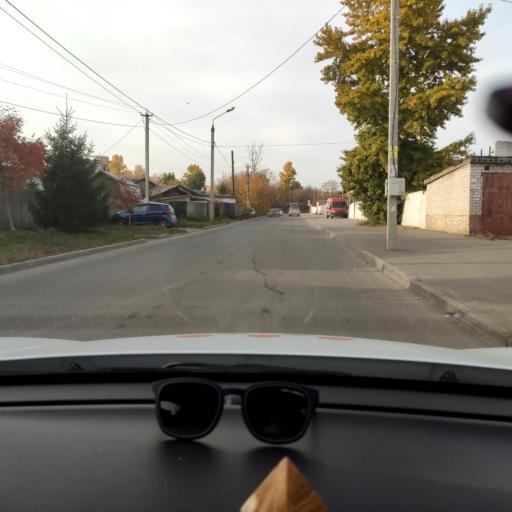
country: RU
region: Tatarstan
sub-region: Gorod Kazan'
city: Kazan
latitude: 55.8058
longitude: 49.0615
